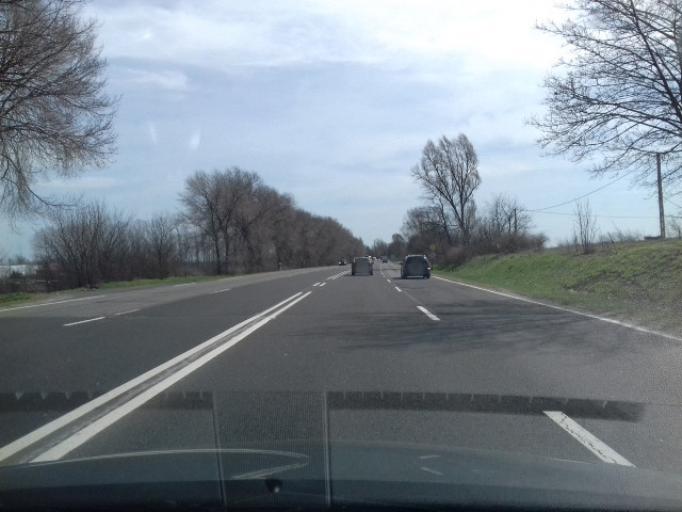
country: HU
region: Bacs-Kiskun
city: Kecskemet
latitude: 46.9705
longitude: 19.6341
